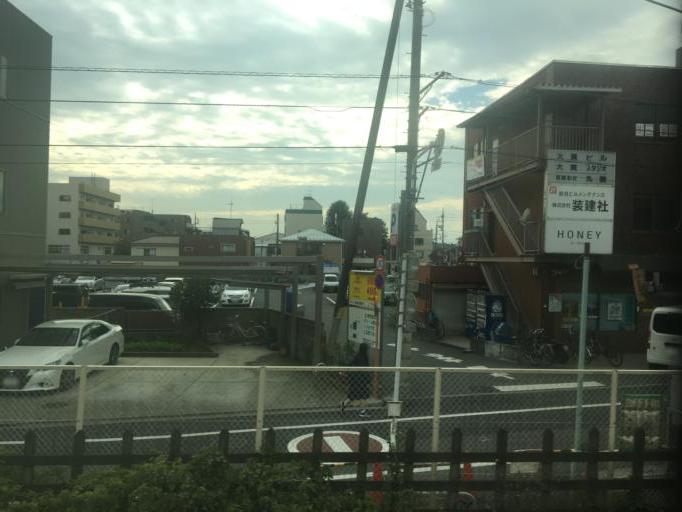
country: JP
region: Tokyo
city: Fussa
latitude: 35.7128
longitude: 139.3634
